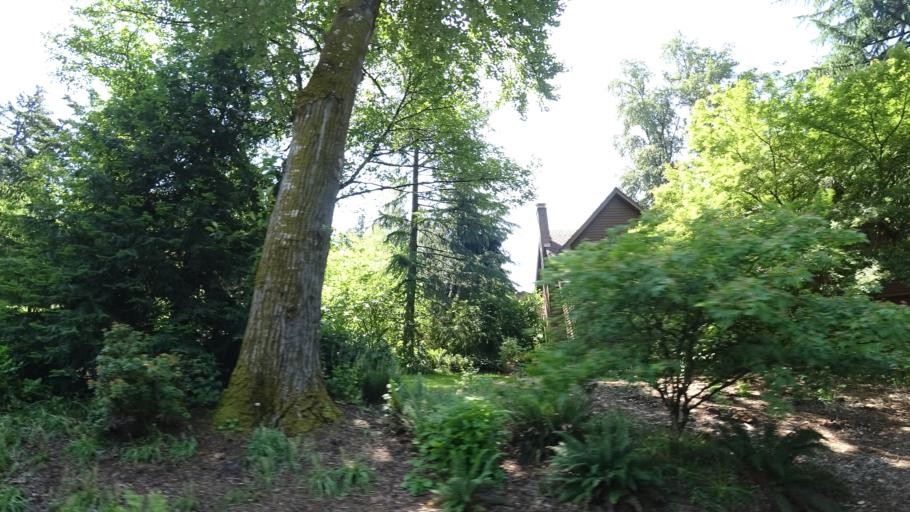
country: US
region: Oregon
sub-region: Washington County
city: Metzger
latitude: 45.4390
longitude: -122.7141
